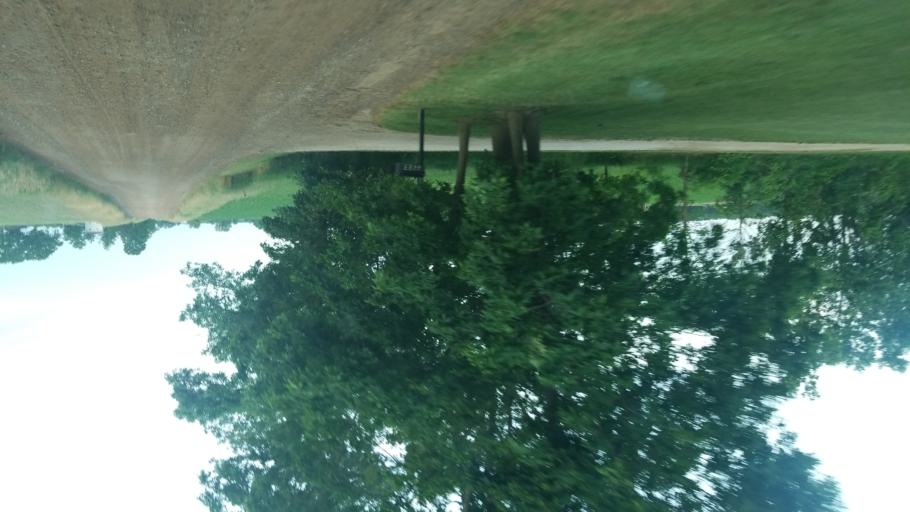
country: US
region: Michigan
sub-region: Eaton County
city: Charlotte
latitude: 42.5973
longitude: -84.9246
